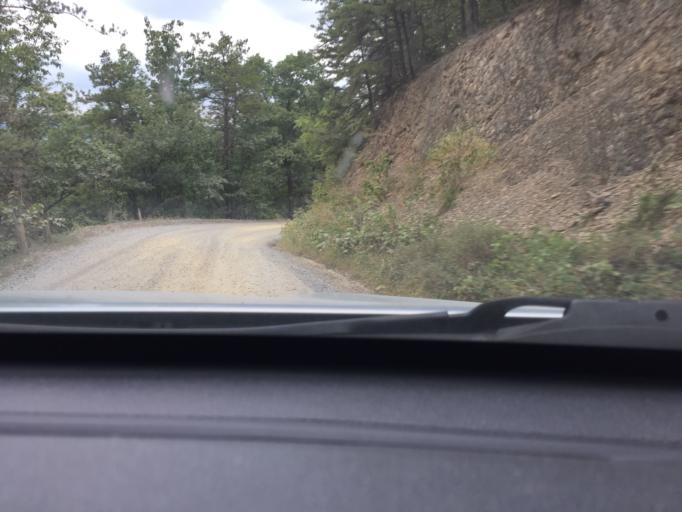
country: US
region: Virginia
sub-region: Shenandoah County
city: Woodstock
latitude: 38.8757
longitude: -78.4639
